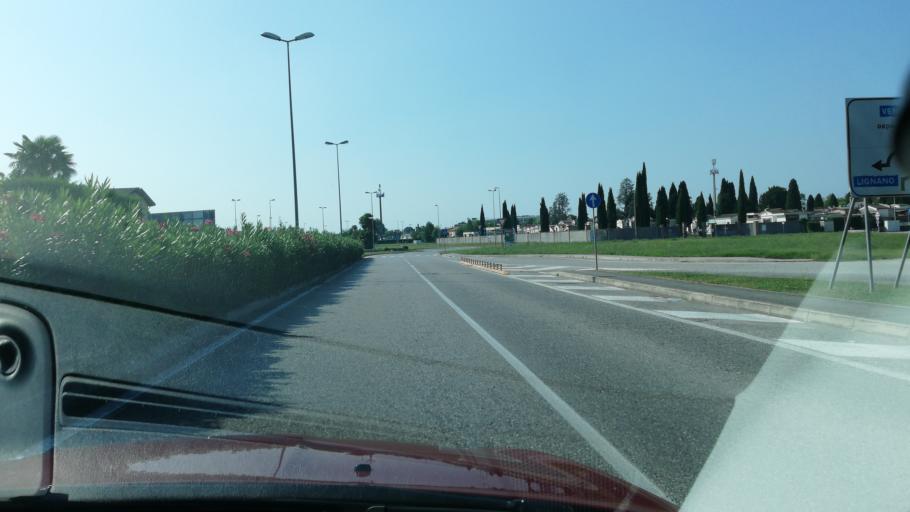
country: IT
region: Friuli Venezia Giulia
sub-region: Provincia di Udine
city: Latisana
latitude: 45.7771
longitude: 13.0029
